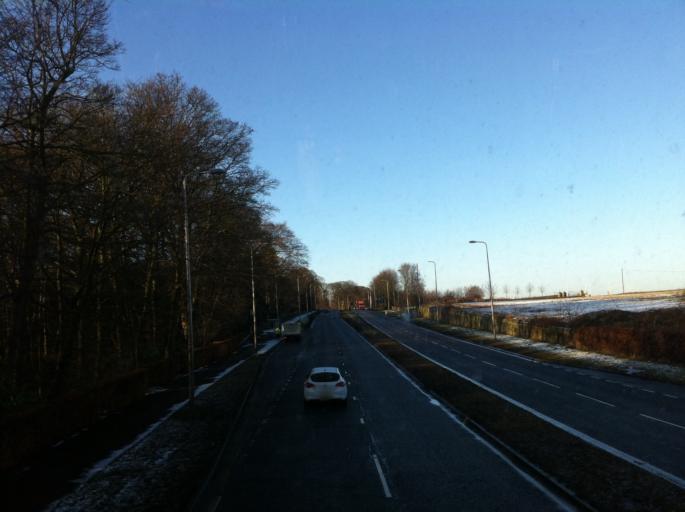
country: GB
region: Scotland
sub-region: Edinburgh
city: Ratho
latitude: 55.9367
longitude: -3.3368
